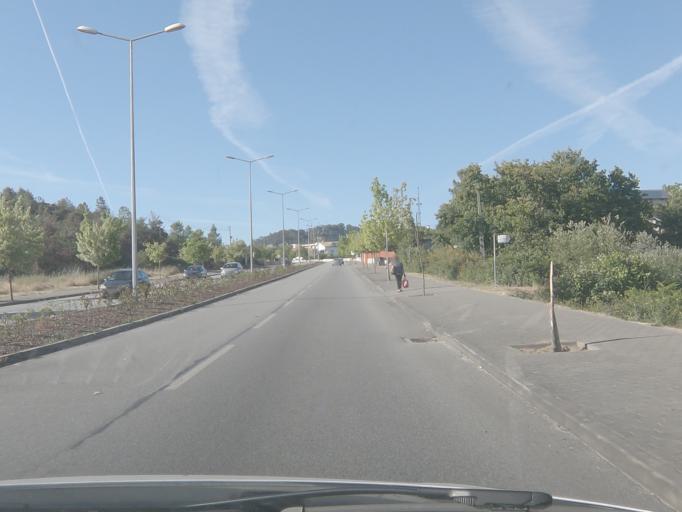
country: PT
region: Viseu
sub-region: Viseu
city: Abraveses
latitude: 40.6819
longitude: -7.9274
